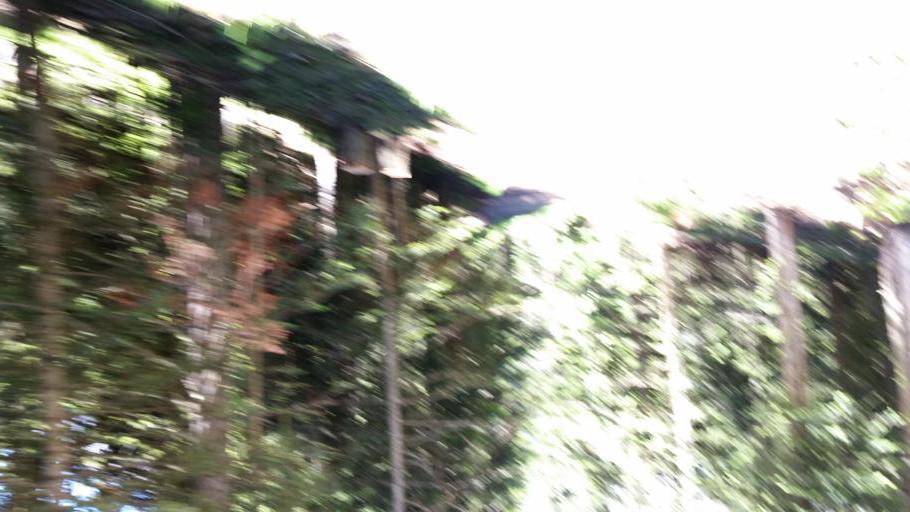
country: CH
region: Valais
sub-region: Martigny District
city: Saillon
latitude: 46.2072
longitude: 7.1756
